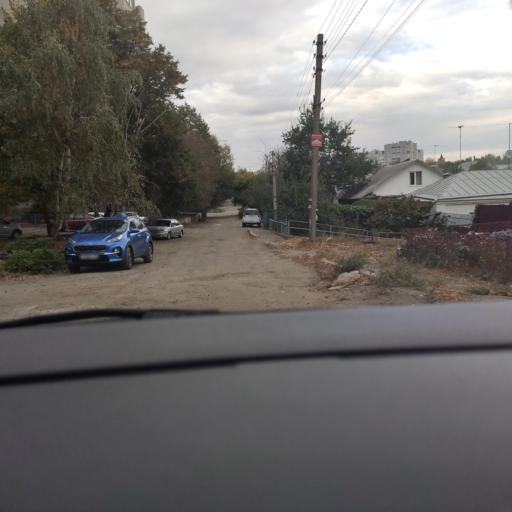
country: RU
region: Voronezj
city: Voronezh
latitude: 51.6898
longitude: 39.1990
